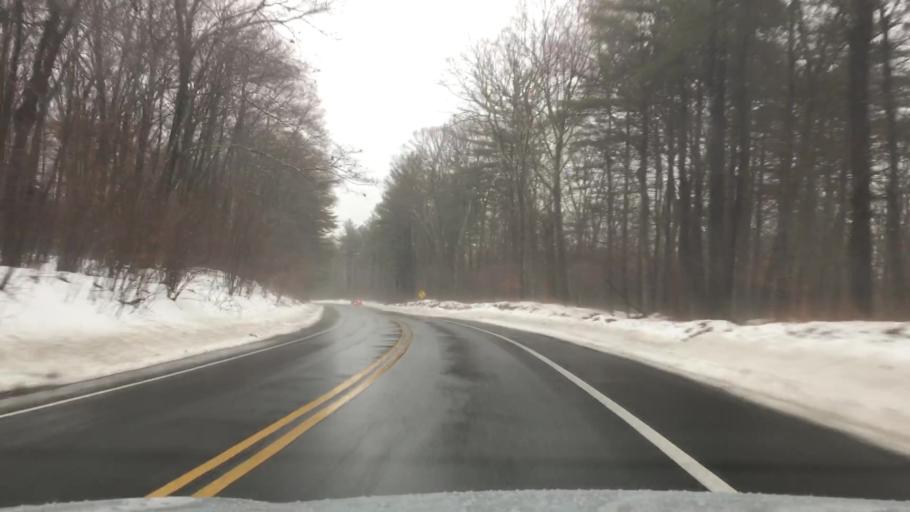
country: US
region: Massachusetts
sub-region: Hampshire County
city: Pelham
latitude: 42.4158
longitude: -72.3995
